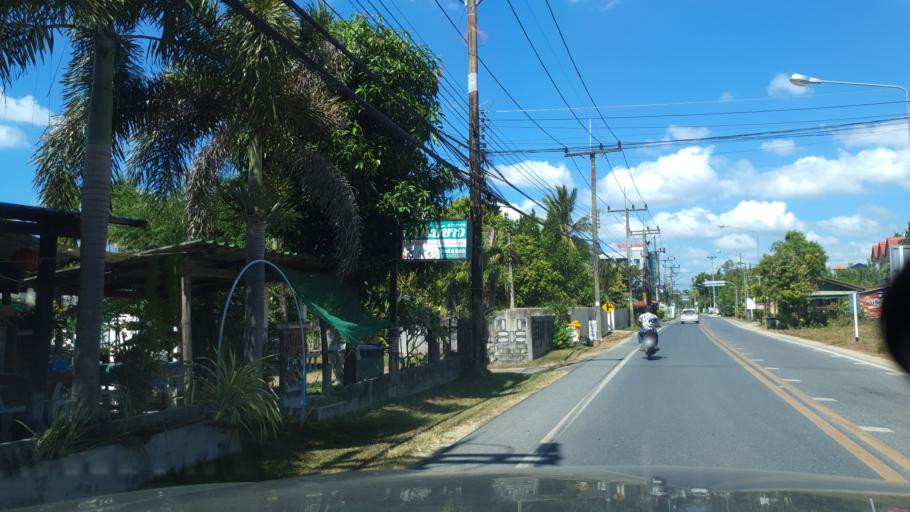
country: TH
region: Phuket
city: Thalang
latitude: 8.1332
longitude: 98.3073
